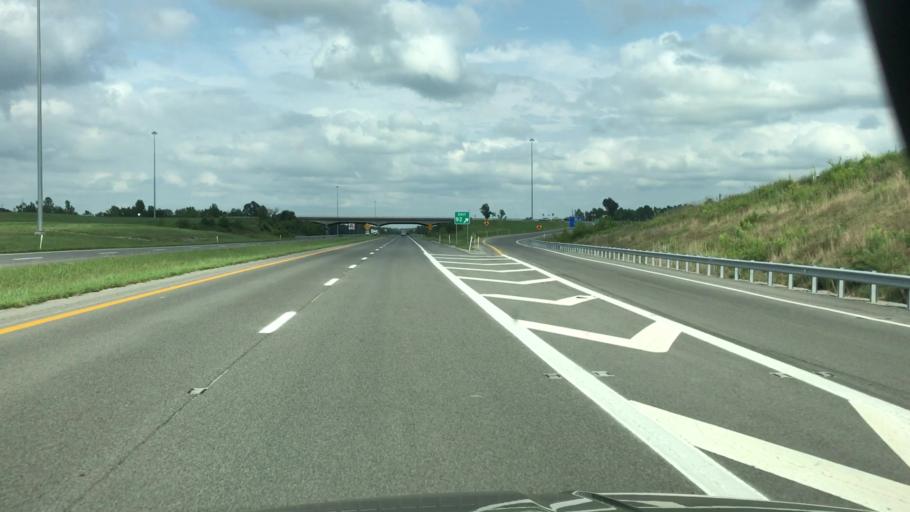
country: US
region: Kentucky
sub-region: Hopkins County
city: Dawson Springs
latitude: 37.1976
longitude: -87.6931
